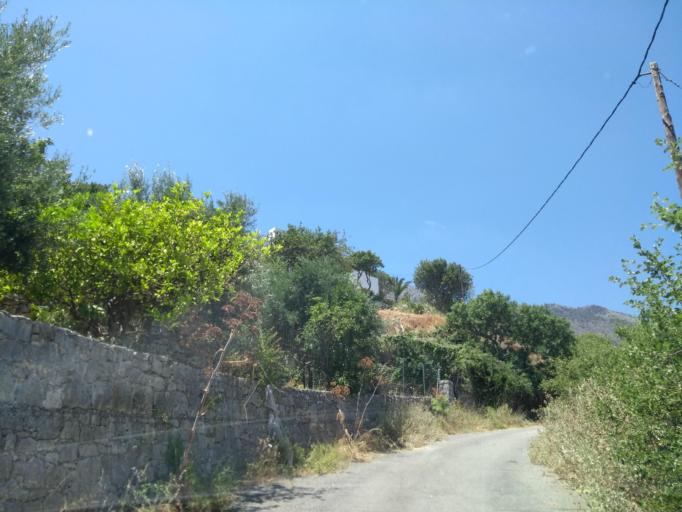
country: GR
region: Crete
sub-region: Nomos Chanias
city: Georgioupolis
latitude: 35.3158
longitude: 24.2893
